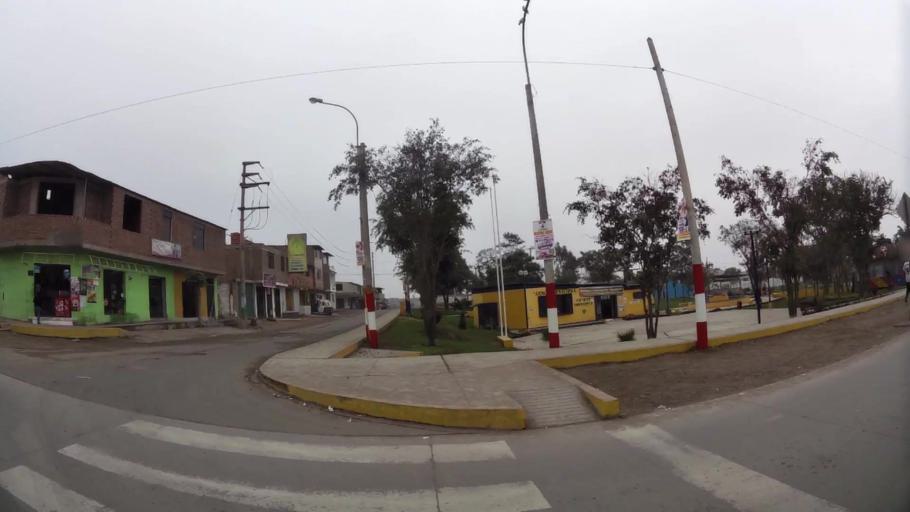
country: PE
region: Lima
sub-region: Lima
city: Surco
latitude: -12.1878
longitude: -76.9254
